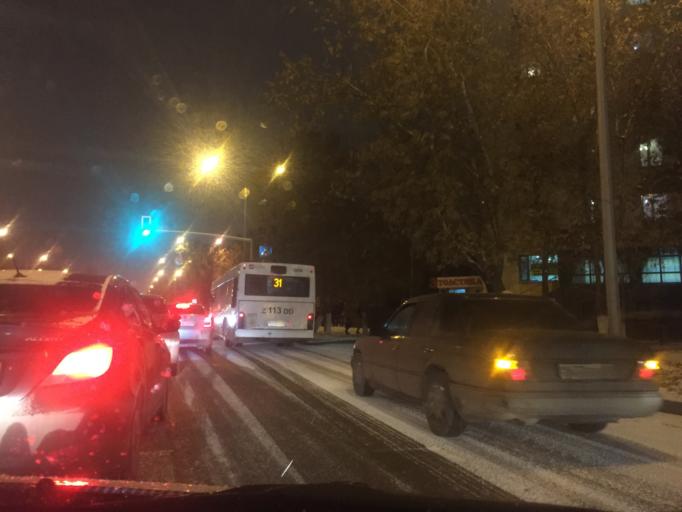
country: KZ
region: Astana Qalasy
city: Astana
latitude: 51.1796
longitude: 71.4099
